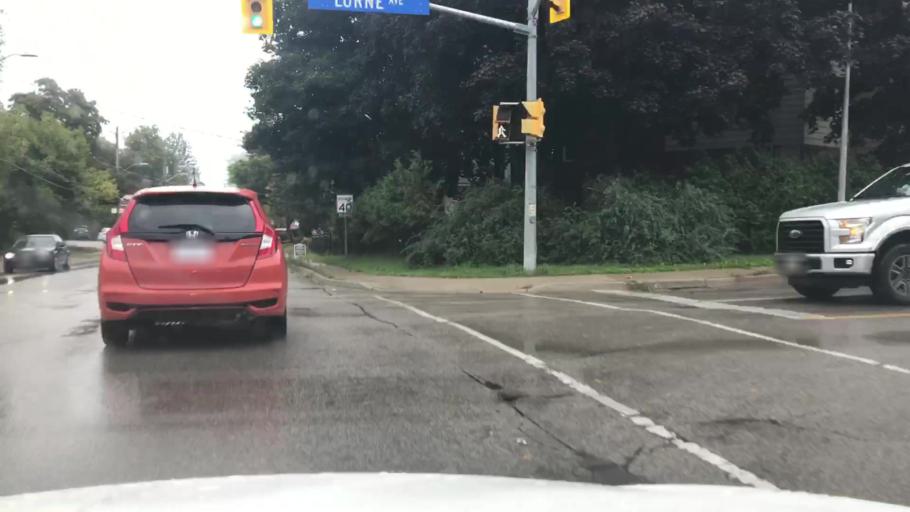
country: CA
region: Ontario
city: Newmarket
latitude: 44.0487
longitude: -79.4630
